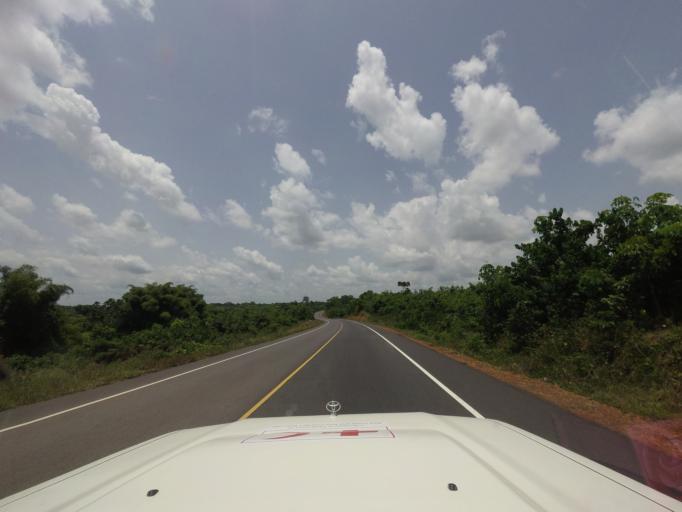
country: LR
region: Margibi
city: Kakata
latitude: 6.5156
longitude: -10.3885
